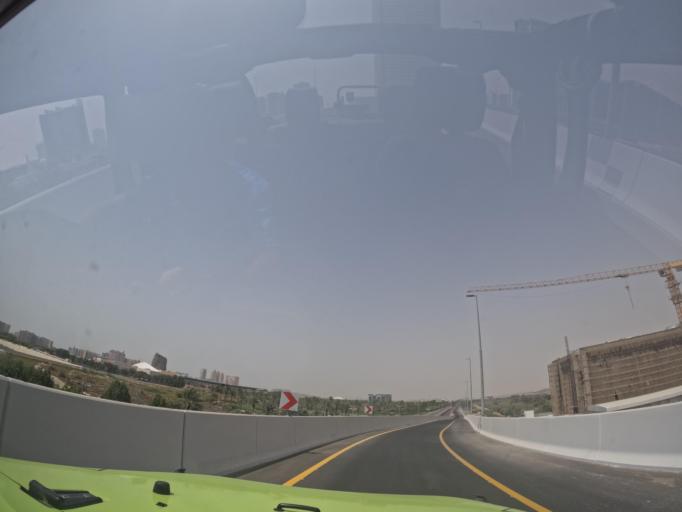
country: AE
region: Dubai
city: Dubai
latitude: 25.0974
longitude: 55.3848
